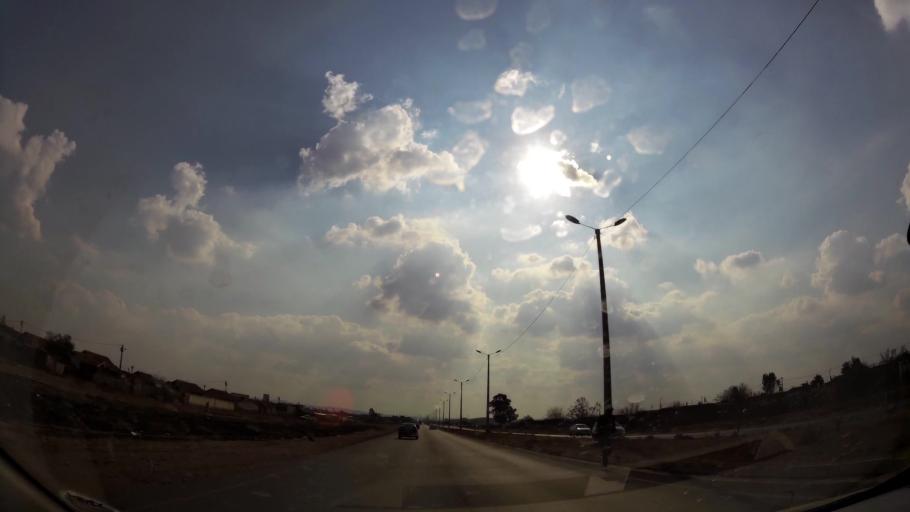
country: ZA
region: Gauteng
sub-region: Ekurhuleni Metropolitan Municipality
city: Germiston
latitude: -26.3142
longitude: 28.2064
